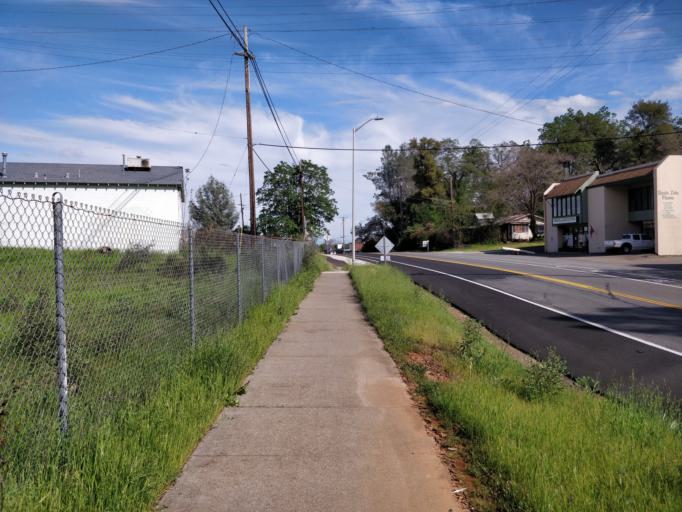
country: US
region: California
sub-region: Shasta County
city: Central Valley (historical)
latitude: 40.6818
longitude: -122.3751
